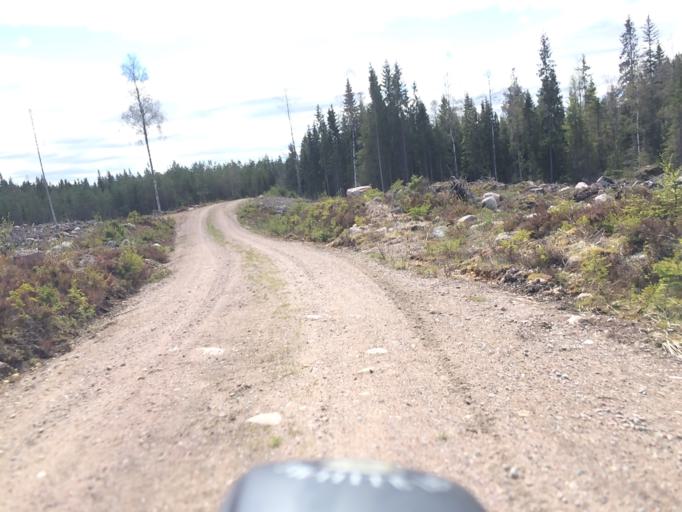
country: SE
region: OErebro
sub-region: Hallefors Kommun
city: Haellefors
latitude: 60.0500
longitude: 14.5155
